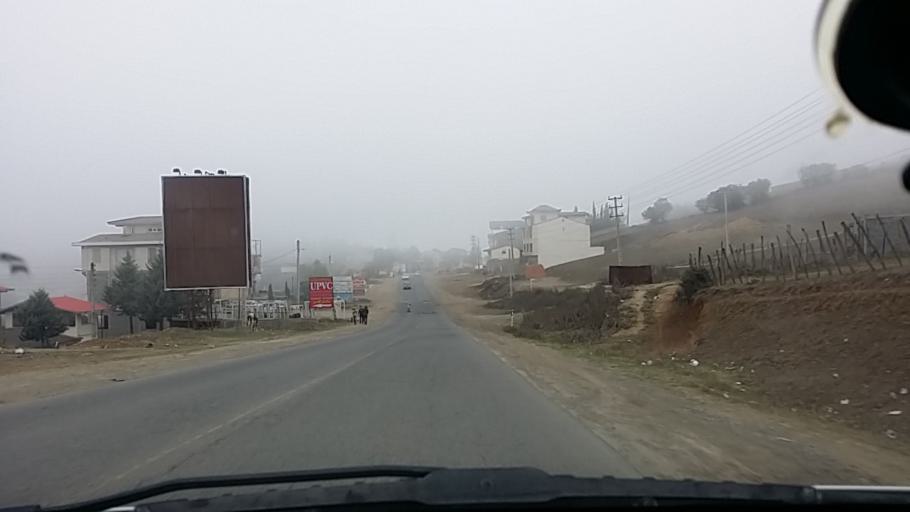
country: IR
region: Mazandaran
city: Chalus
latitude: 36.5149
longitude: 51.2460
